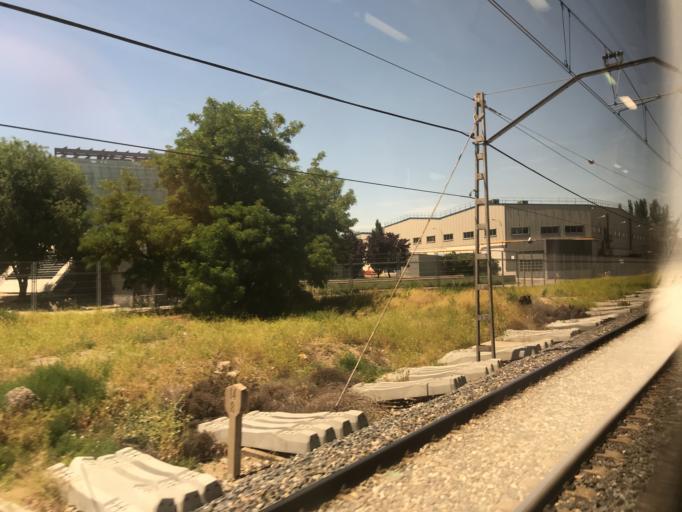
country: ES
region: Madrid
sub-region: Provincia de Madrid
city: Getafe
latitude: 40.2962
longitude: -3.7062
